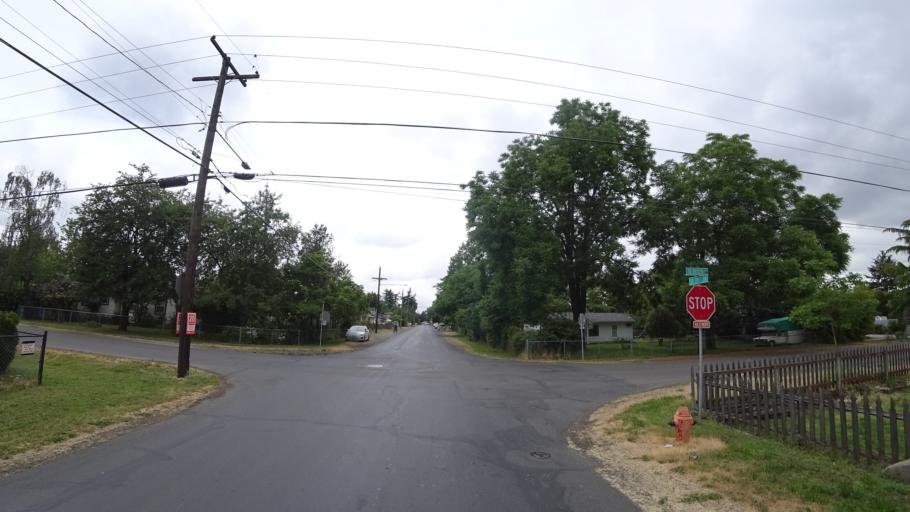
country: US
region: Oregon
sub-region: Multnomah County
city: Lents
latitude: 45.4708
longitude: -122.5830
